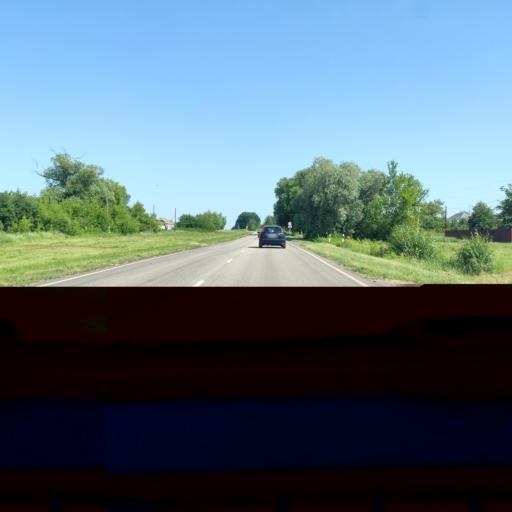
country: RU
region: Voronezj
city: Verkhnyaya Khava
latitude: 51.6700
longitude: 39.9579
